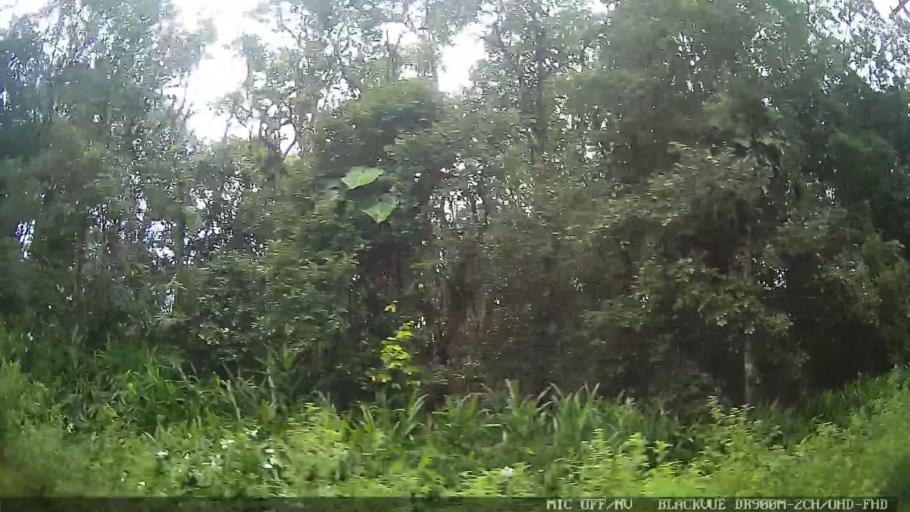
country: BR
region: Sao Paulo
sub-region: Peruibe
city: Peruibe
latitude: -24.2210
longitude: -46.9210
